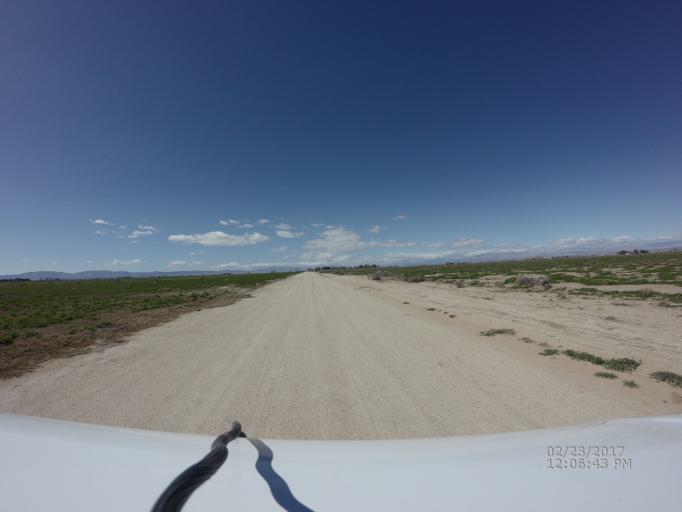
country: US
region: California
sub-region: Los Angeles County
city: Lancaster
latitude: 34.7414
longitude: -118.0069
